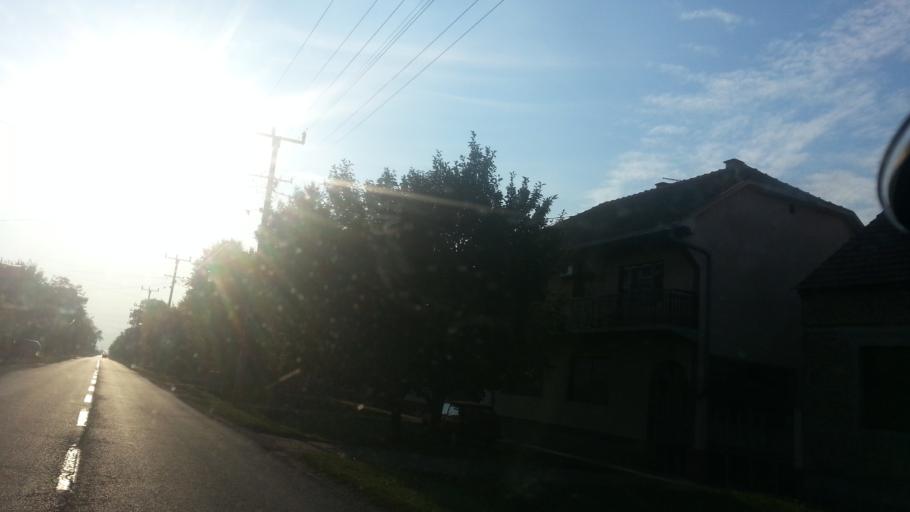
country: RS
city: Novi Karlovci
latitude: 45.0781
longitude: 20.1680
